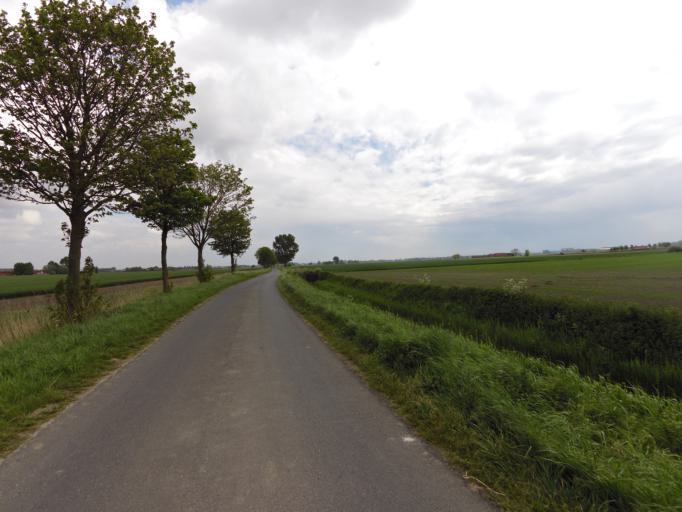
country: BE
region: Flanders
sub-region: Provincie West-Vlaanderen
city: Gistel
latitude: 51.1159
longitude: 2.8959
